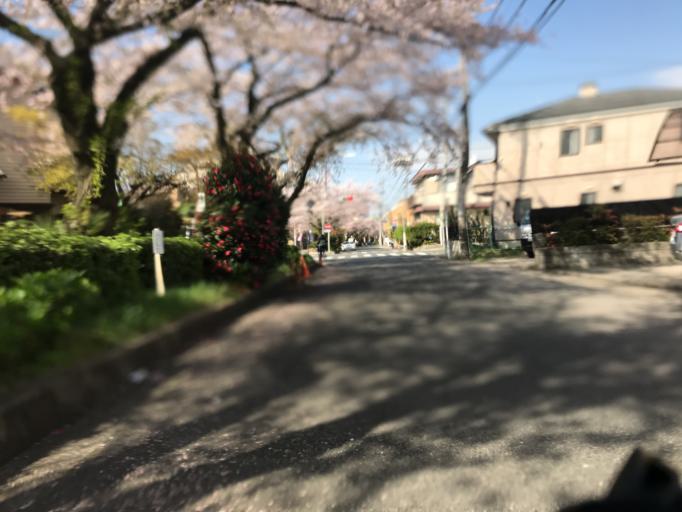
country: JP
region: Aichi
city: Nagoya-shi
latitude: 35.1721
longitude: 136.9446
